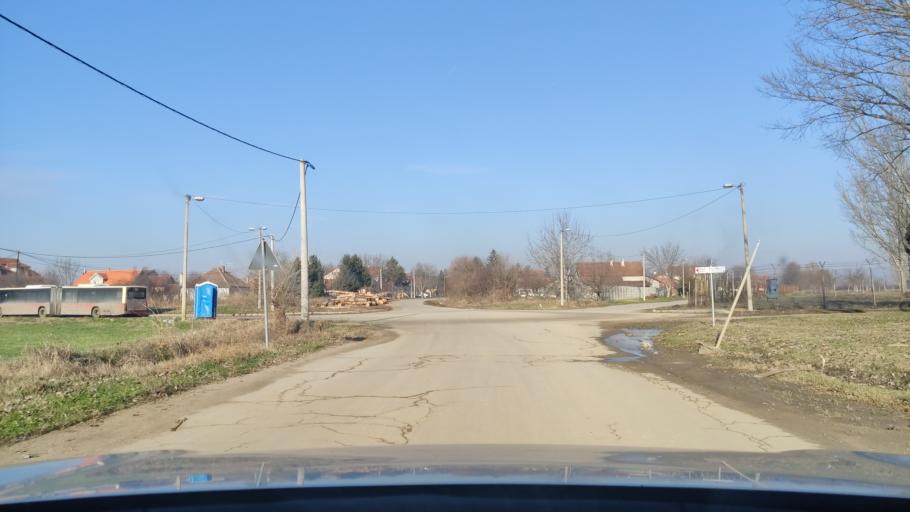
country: RS
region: Central Serbia
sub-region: Belgrade
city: Surcin
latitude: 44.7450
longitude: 20.2714
